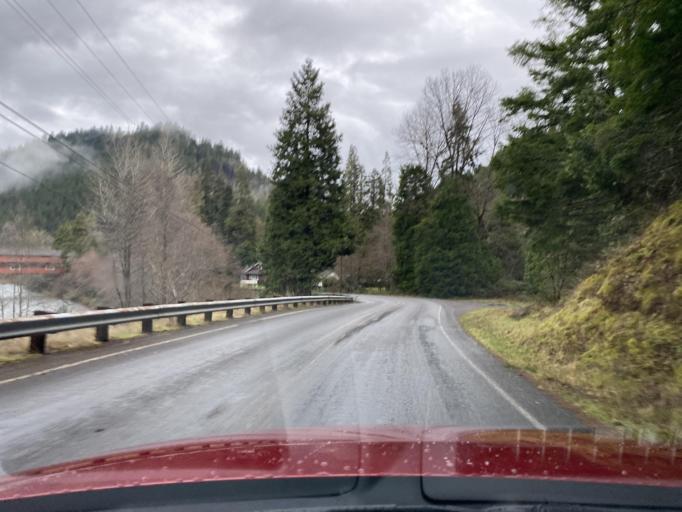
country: US
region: Oregon
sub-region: Lane County
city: Oakridge
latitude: 43.7571
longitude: -122.4978
